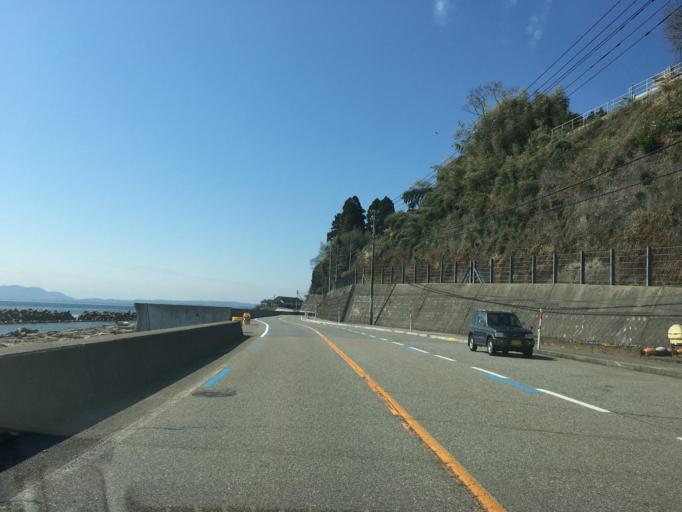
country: JP
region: Toyama
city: Himi
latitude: 36.9032
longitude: 137.0131
